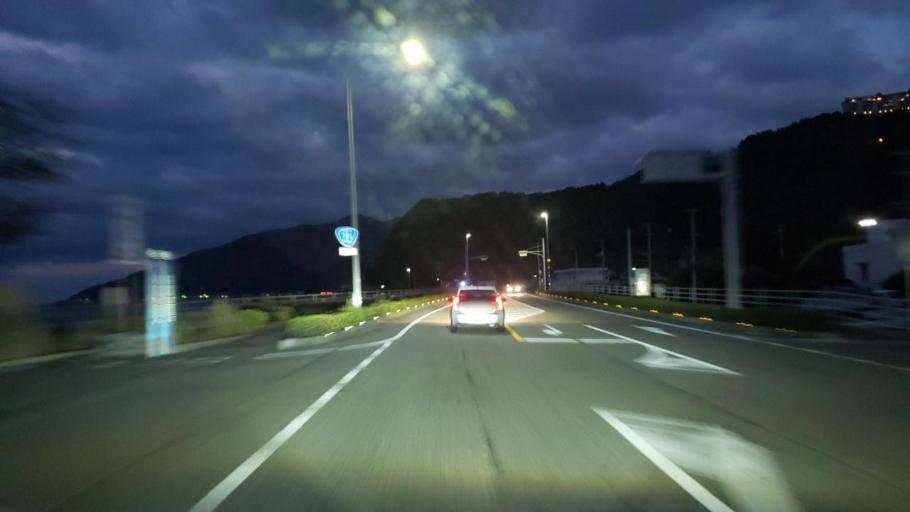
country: JP
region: Tokushima
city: Ishii
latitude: 34.2073
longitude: 134.4621
